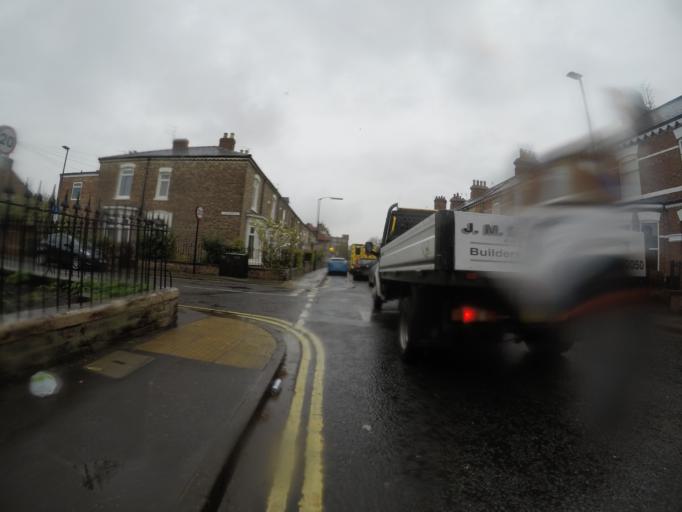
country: GB
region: England
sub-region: City of York
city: York
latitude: 53.9710
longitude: -1.0779
